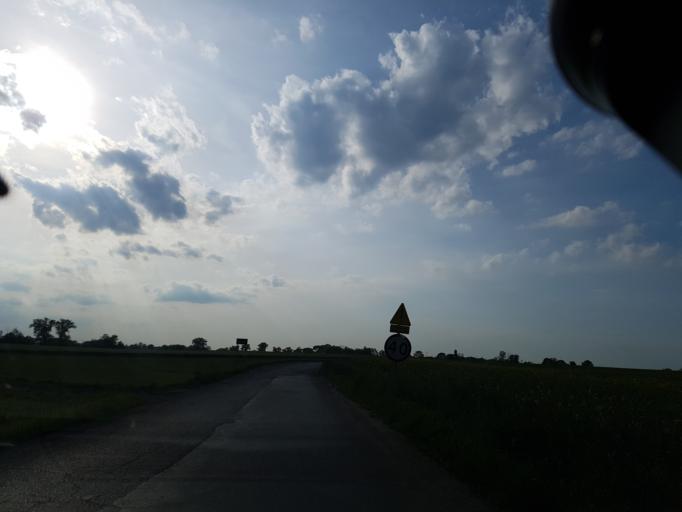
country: PL
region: Lower Silesian Voivodeship
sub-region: Powiat wroclawski
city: Zorawina
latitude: 50.9102
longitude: 17.0037
